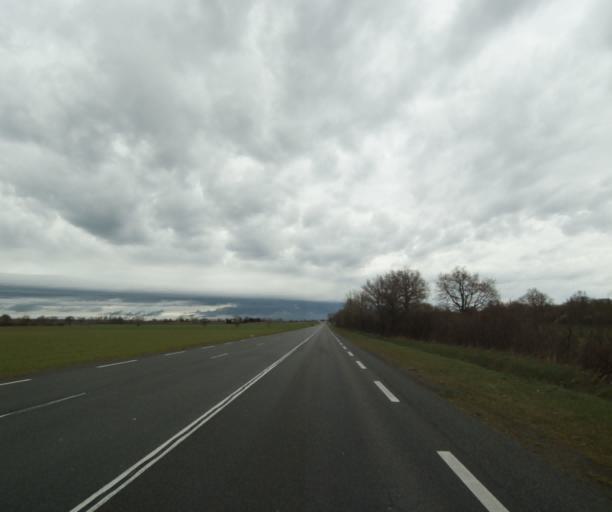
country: FR
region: Auvergne
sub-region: Departement de l'Allier
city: Toulon-sur-Allier
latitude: 46.4819
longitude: 3.3663
